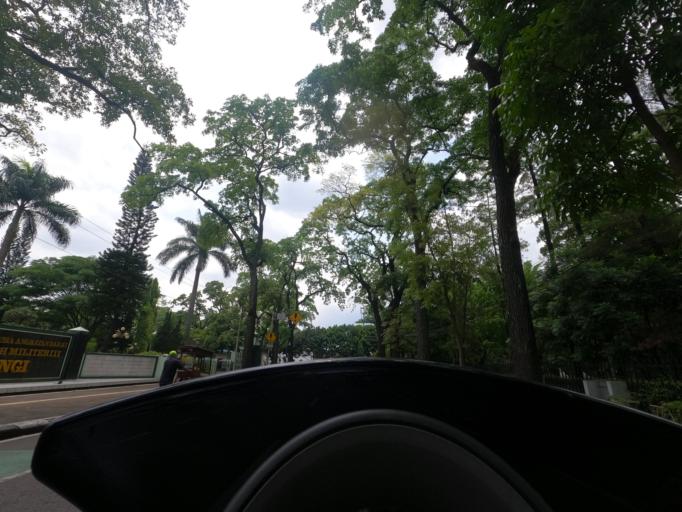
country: ID
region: West Java
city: Bandung
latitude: -6.9102
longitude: 107.6133
